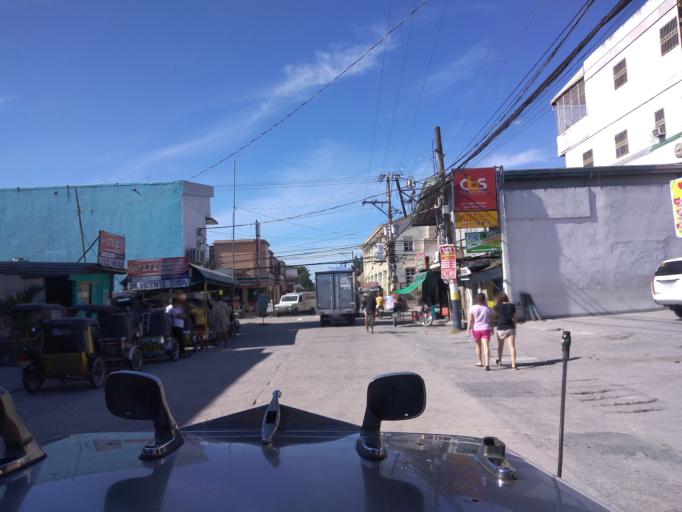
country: PH
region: Central Luzon
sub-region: Province of Pampanga
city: Santa Rita
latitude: 14.9979
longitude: 120.6147
